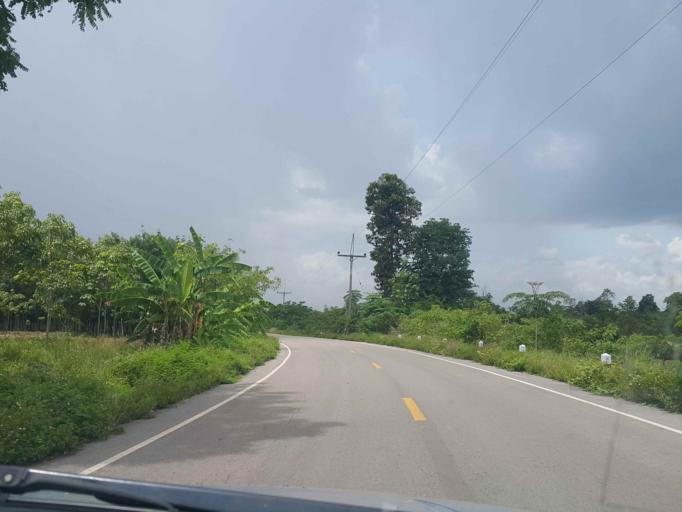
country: TH
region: Phayao
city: Dok Kham Tai
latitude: 19.0472
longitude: 99.9511
